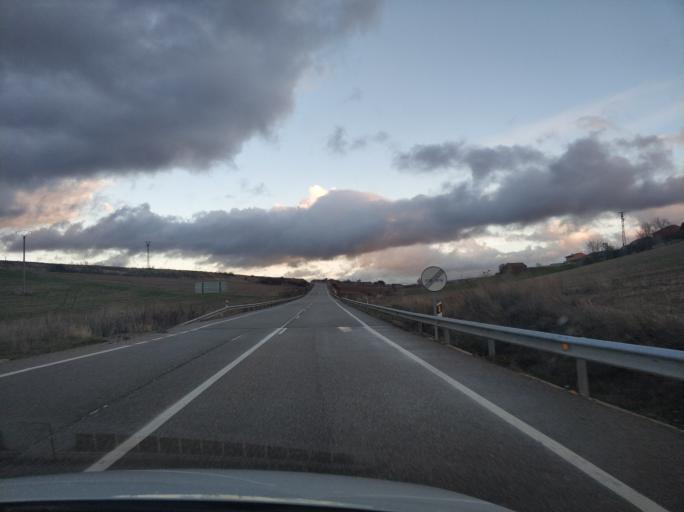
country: ES
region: Castille and Leon
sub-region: Provincia de Segovia
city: Ayllon
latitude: 41.4161
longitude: -3.4054
